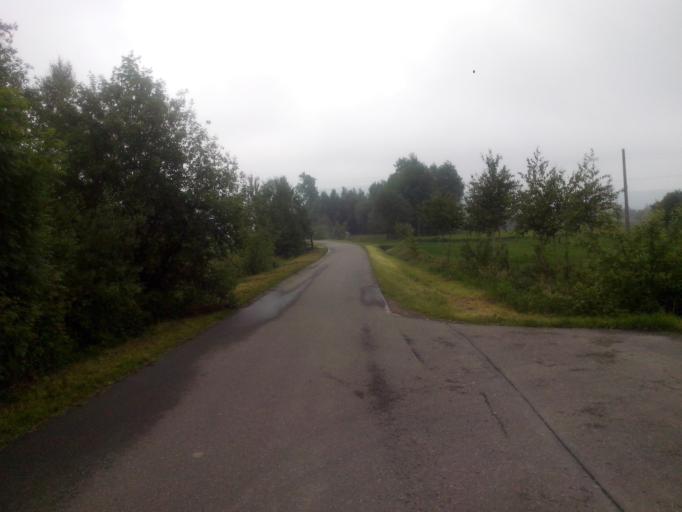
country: PL
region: Subcarpathian Voivodeship
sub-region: Powiat strzyzowski
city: Wysoka Strzyzowska
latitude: 49.8085
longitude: 21.7819
